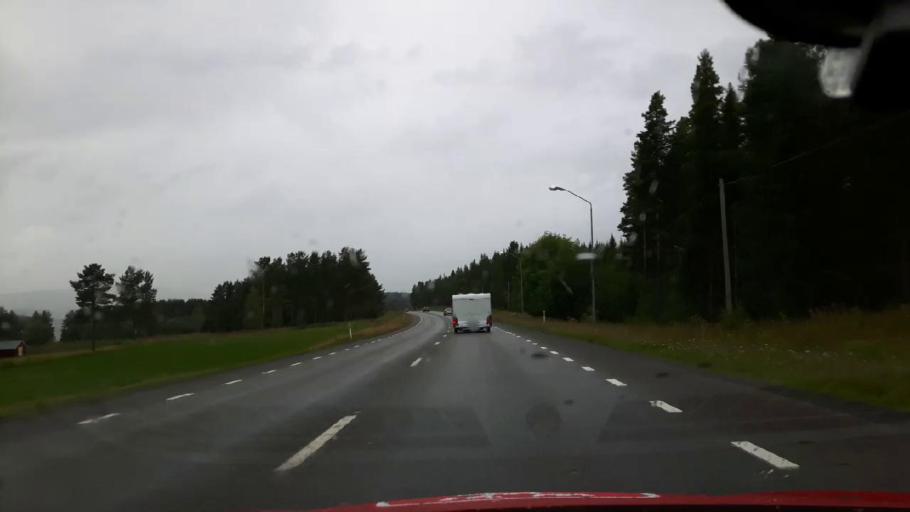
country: SE
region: Jaemtland
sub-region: Are Kommun
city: Jarpen
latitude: 63.3267
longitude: 13.5359
